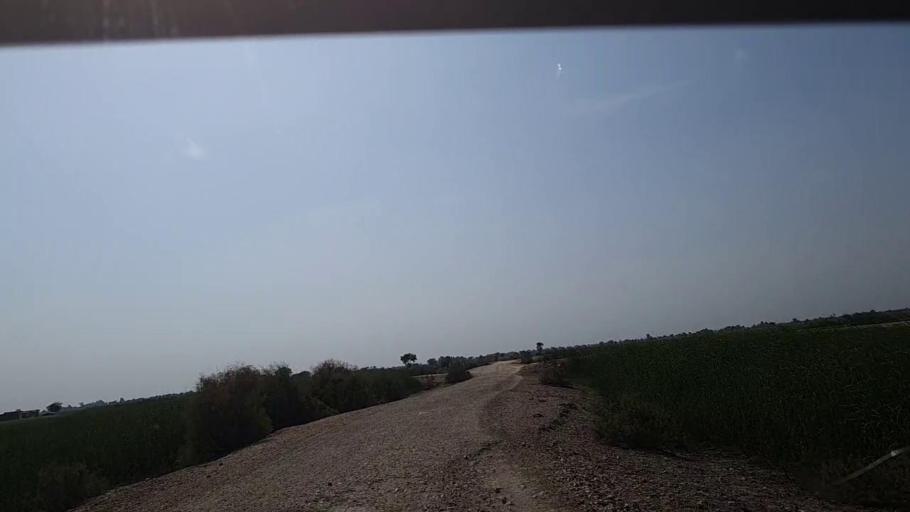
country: PK
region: Sindh
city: Khanpur
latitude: 27.8487
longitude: 69.3698
